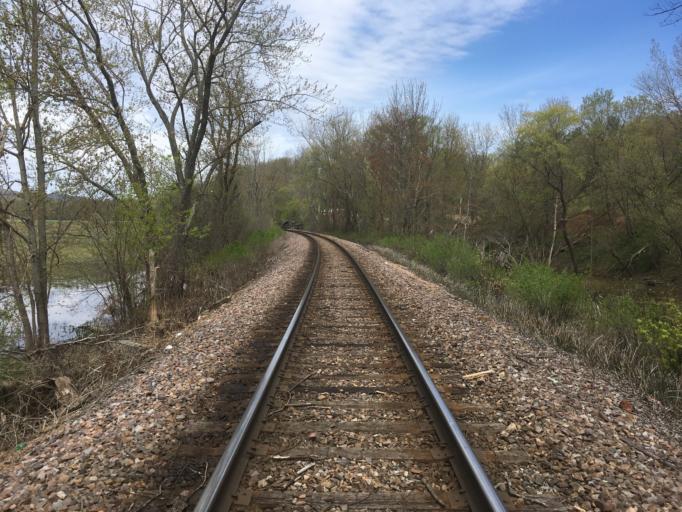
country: US
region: Vermont
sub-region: Rutland County
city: Brandon
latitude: 43.7094
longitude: -73.0368
